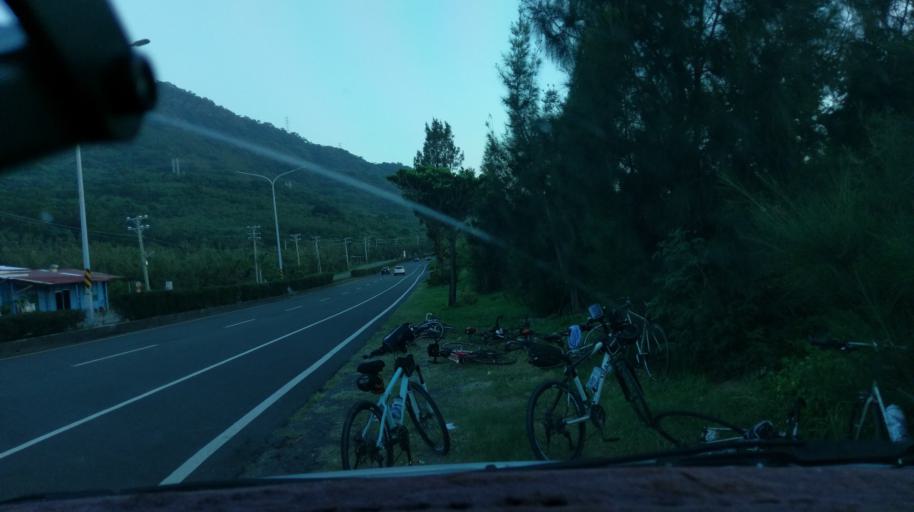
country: TW
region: Taiwan
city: Hengchun
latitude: 22.1808
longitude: 120.6930
